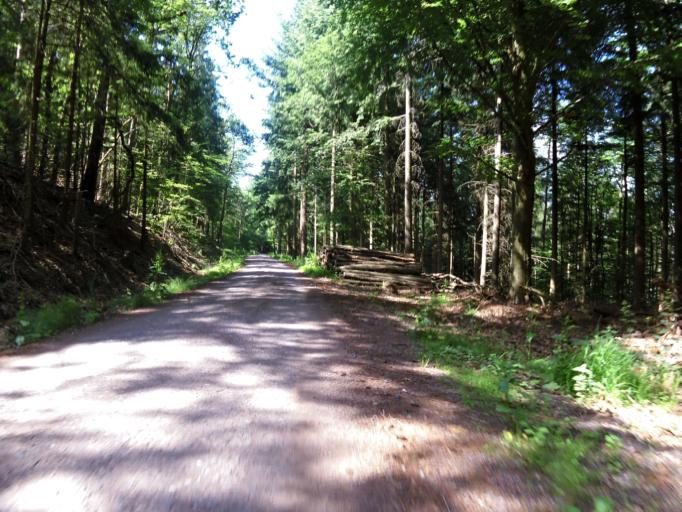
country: DE
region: Rheinland-Pfalz
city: Ramberg
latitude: 49.2973
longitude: 8.0036
